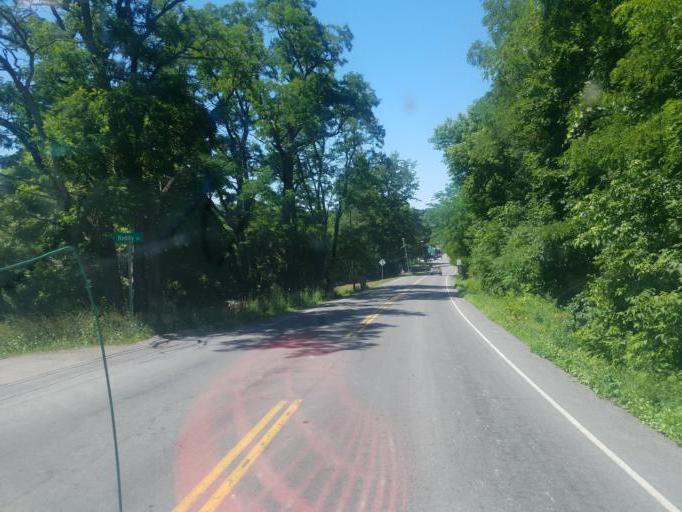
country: US
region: New York
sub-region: Yates County
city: Penn Yan
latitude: 42.7552
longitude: -77.0132
